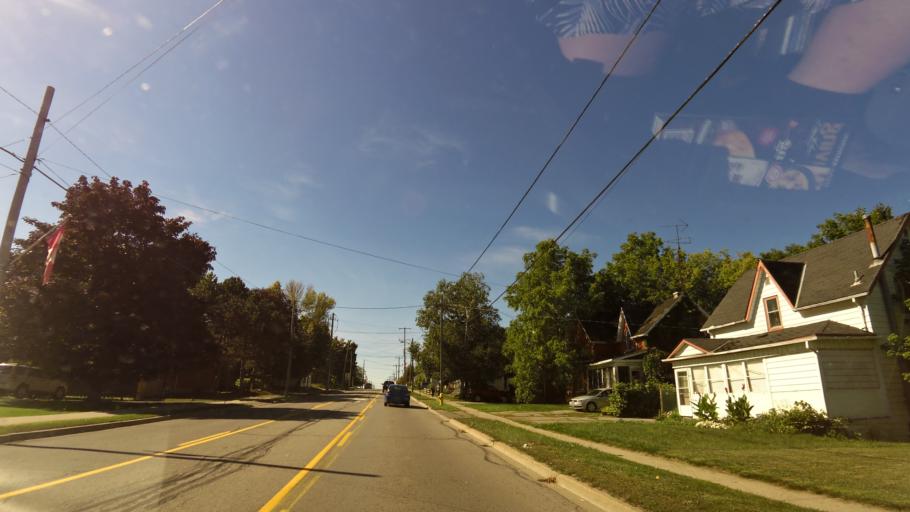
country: CA
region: Ontario
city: Ancaster
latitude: 43.0703
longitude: -79.9538
